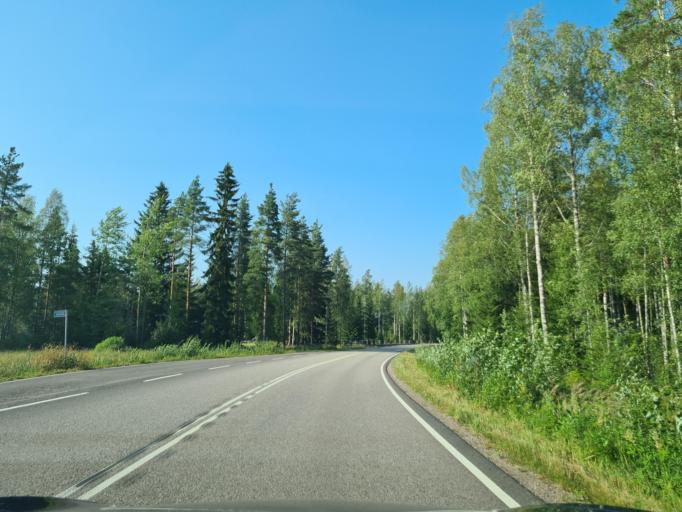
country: FI
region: Satakunta
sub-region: Pohjois-Satakunta
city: Karvia
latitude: 62.2060
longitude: 22.6006
